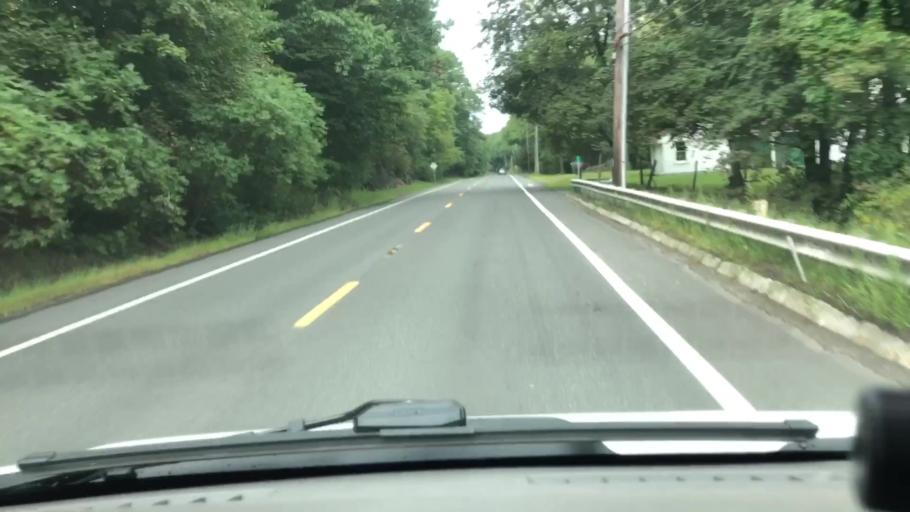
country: US
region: Massachusetts
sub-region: Franklin County
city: Ashfield
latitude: 42.5326
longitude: -72.8055
